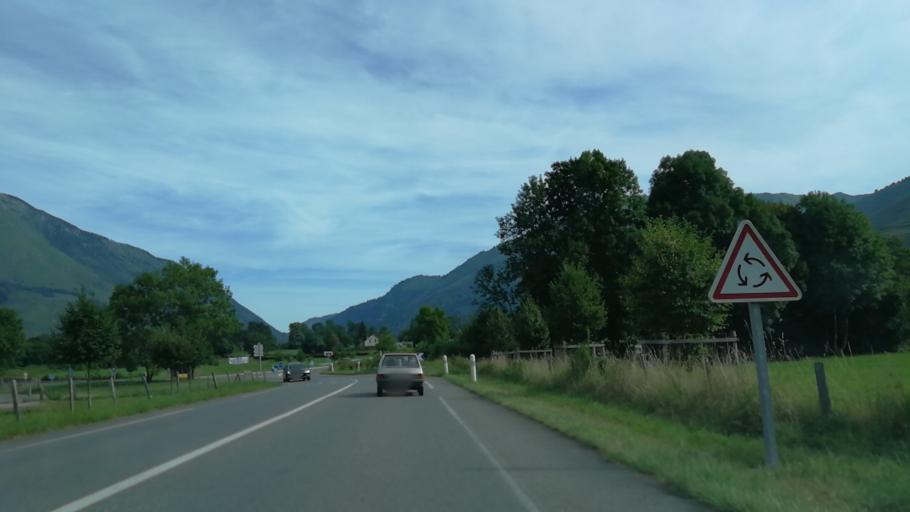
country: FR
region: Aquitaine
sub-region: Departement des Pyrenees-Atlantiques
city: Arette
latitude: 42.9688
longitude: -0.6091
